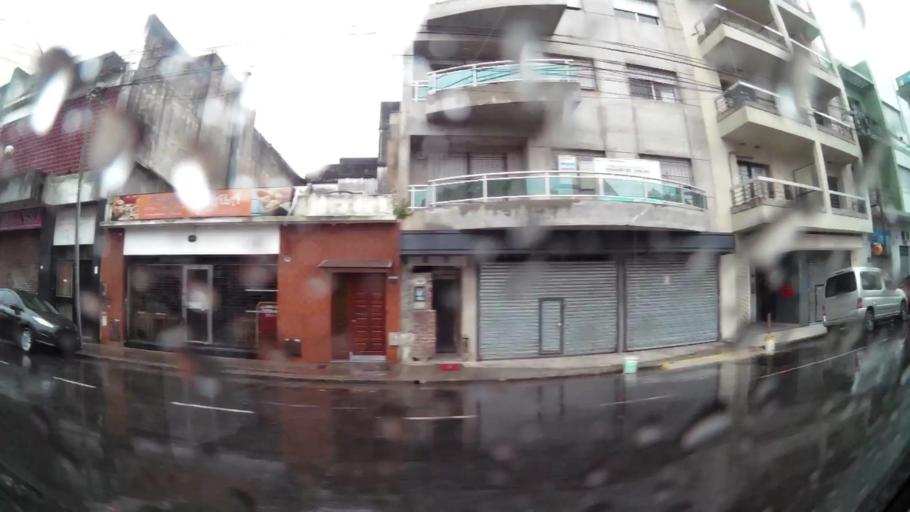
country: AR
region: Buenos Aires
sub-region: Partido de Avellaneda
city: Avellaneda
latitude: -34.6383
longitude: -58.3717
